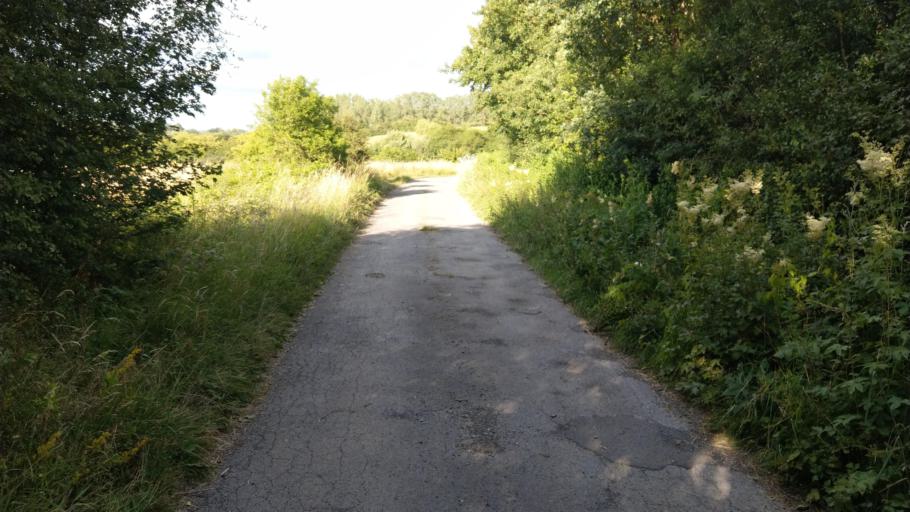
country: BE
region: Wallonia
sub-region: Province de Namur
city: Couvin
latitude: 50.0693
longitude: 4.4507
